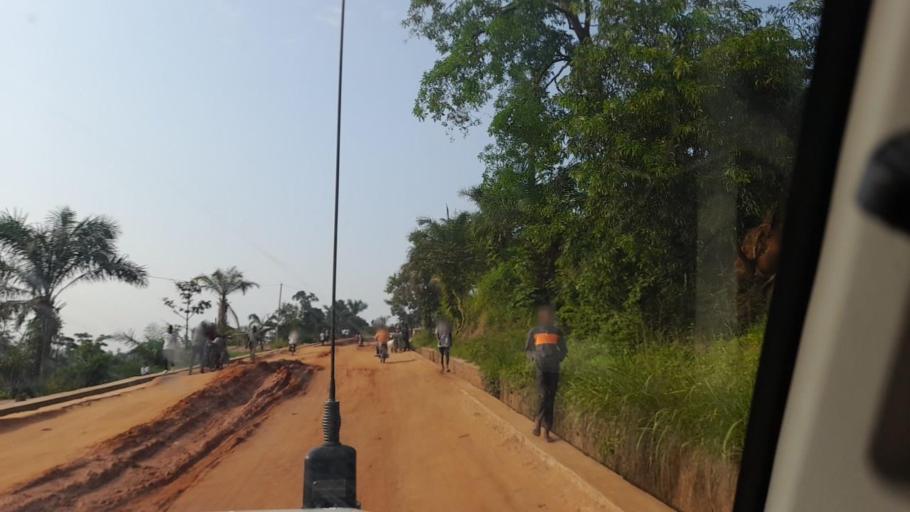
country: CD
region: Kasai-Occidental
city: Kananga
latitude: -5.8966
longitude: 22.3803
